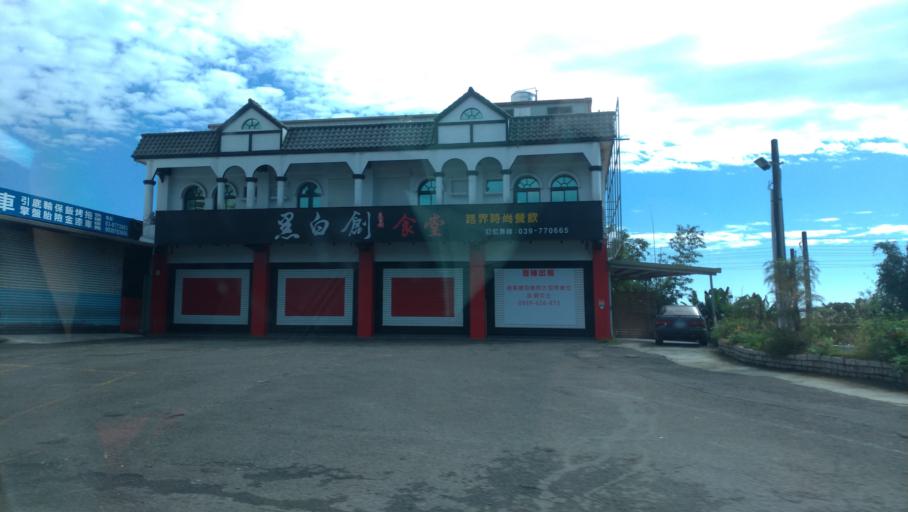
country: TW
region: Taiwan
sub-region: Yilan
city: Yilan
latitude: 24.8501
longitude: 121.8162
